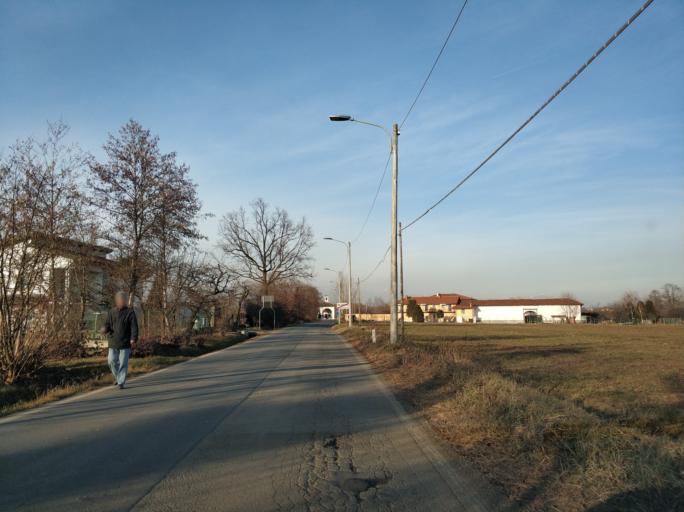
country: IT
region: Piedmont
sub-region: Provincia di Torino
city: San Francesco al Campo
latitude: 45.2087
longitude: 7.6550
